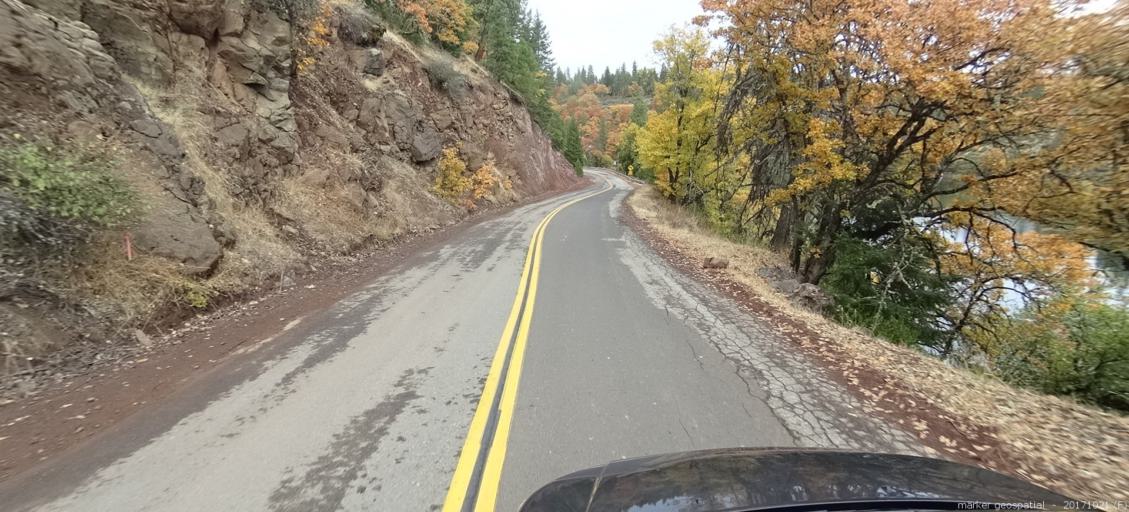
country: US
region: California
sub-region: Shasta County
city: Burney
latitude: 41.0211
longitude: -121.6716
